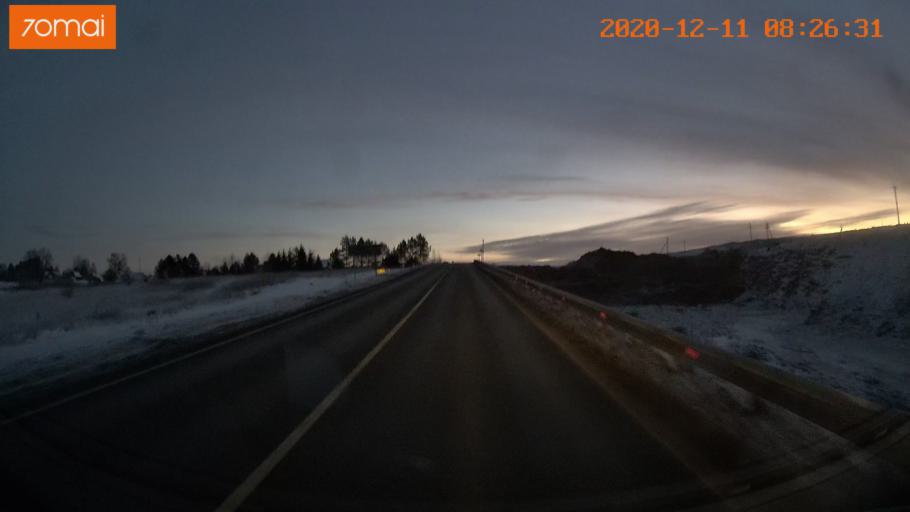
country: RU
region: Vologda
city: Molochnoye
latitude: 59.1704
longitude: 39.4695
